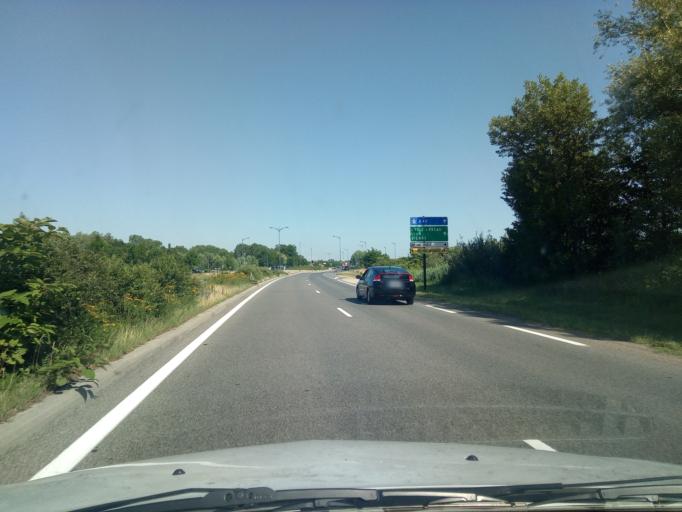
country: FR
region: Rhone-Alpes
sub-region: Departement de l'Isere
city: Domarin
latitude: 45.5952
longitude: 5.2428
